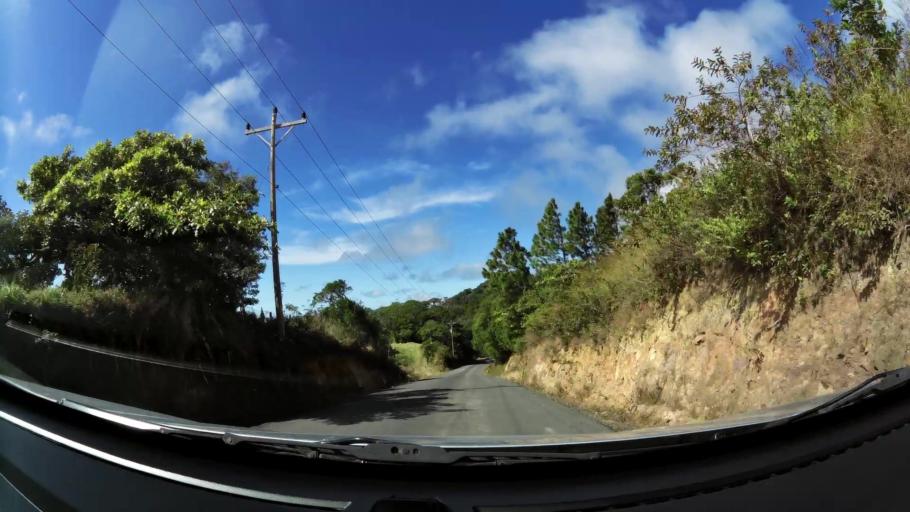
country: CR
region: Guanacaste
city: Juntas
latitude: 10.3394
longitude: -84.8941
